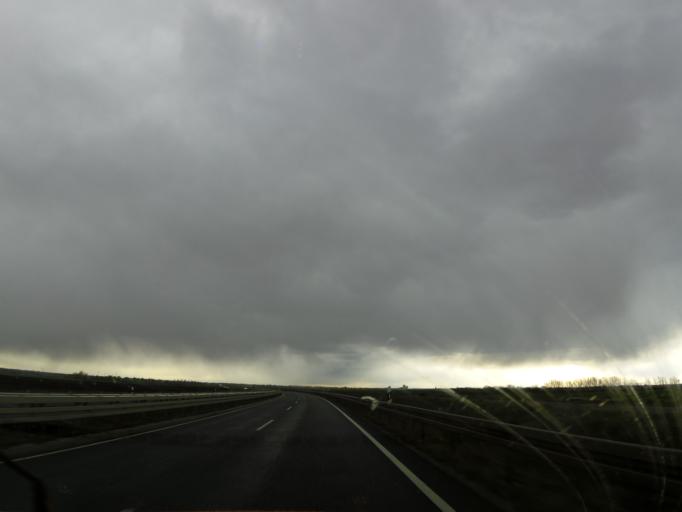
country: DE
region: Saxony-Anhalt
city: Wolmirsleben
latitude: 51.9787
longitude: 11.4749
